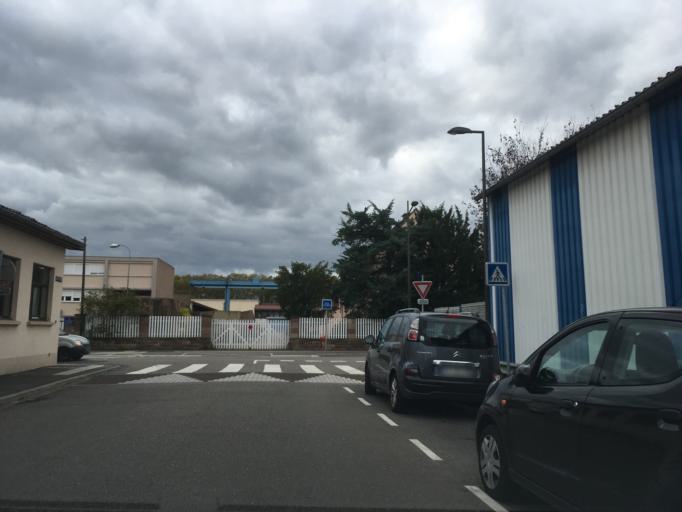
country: FR
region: Alsace
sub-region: Departement du Bas-Rhin
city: Strasbourg
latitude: 48.5571
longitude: 7.7381
